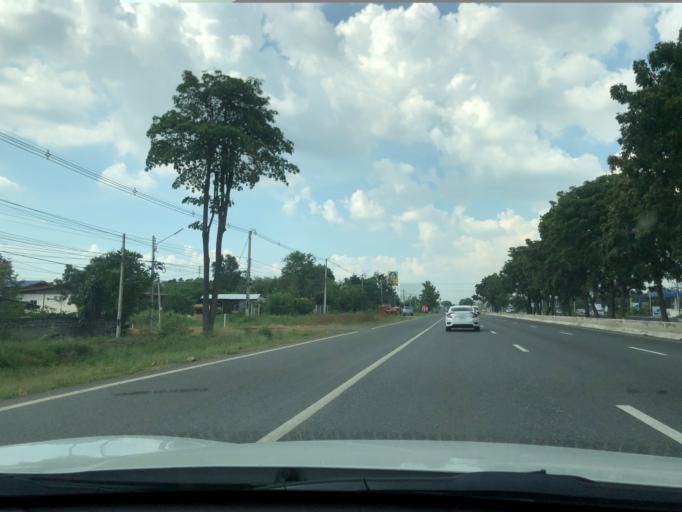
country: TH
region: Nakhon Sawan
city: Krok Phra
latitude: 15.5863
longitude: 100.1239
